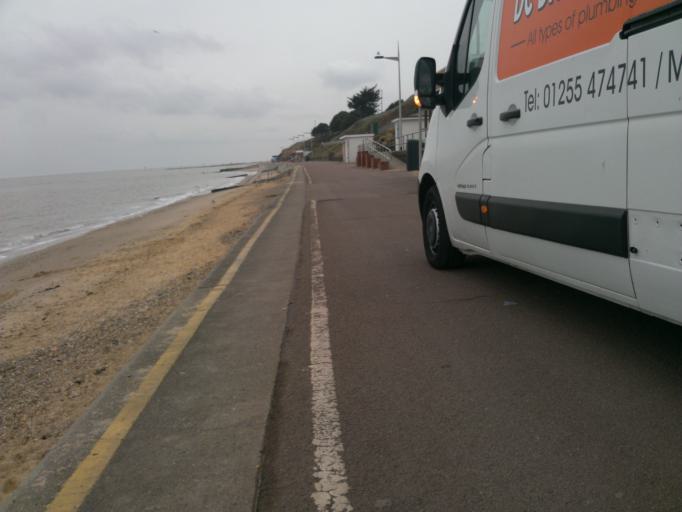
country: GB
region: England
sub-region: Essex
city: Clacton-on-Sea
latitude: 51.7860
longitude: 1.1525
